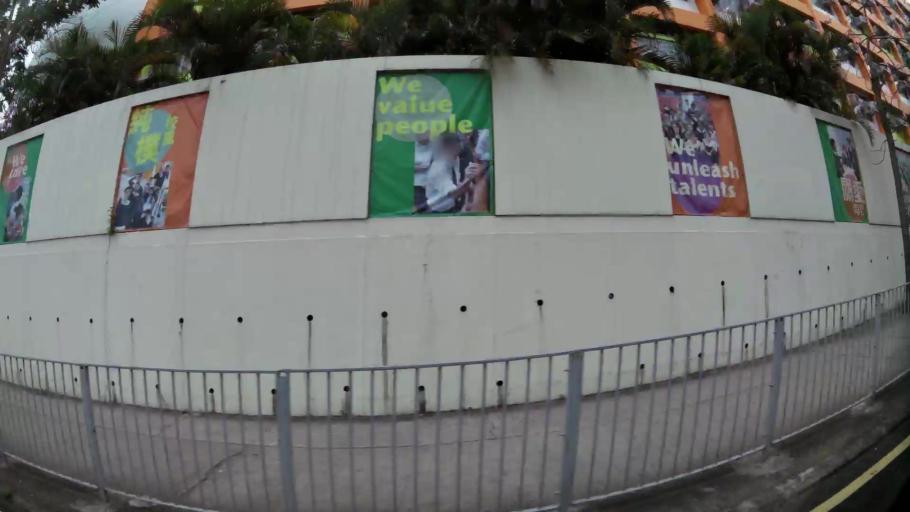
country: HK
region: Kowloon City
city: Kowloon
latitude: 22.3104
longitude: 114.1799
